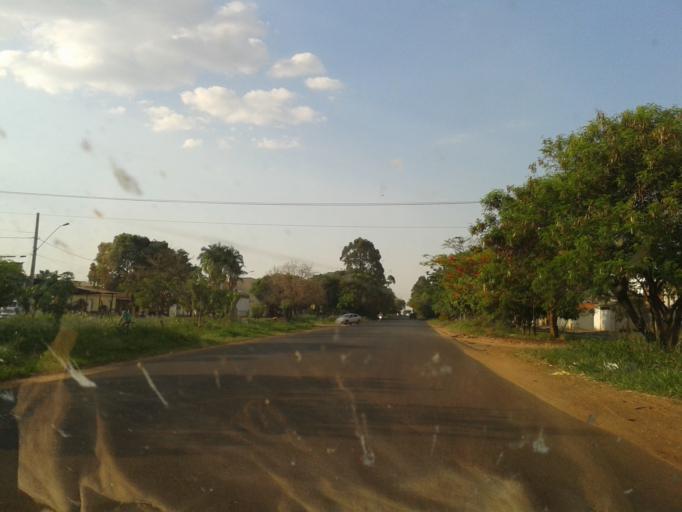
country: BR
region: Minas Gerais
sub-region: Uberlandia
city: Uberlandia
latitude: -18.9470
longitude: -48.3071
